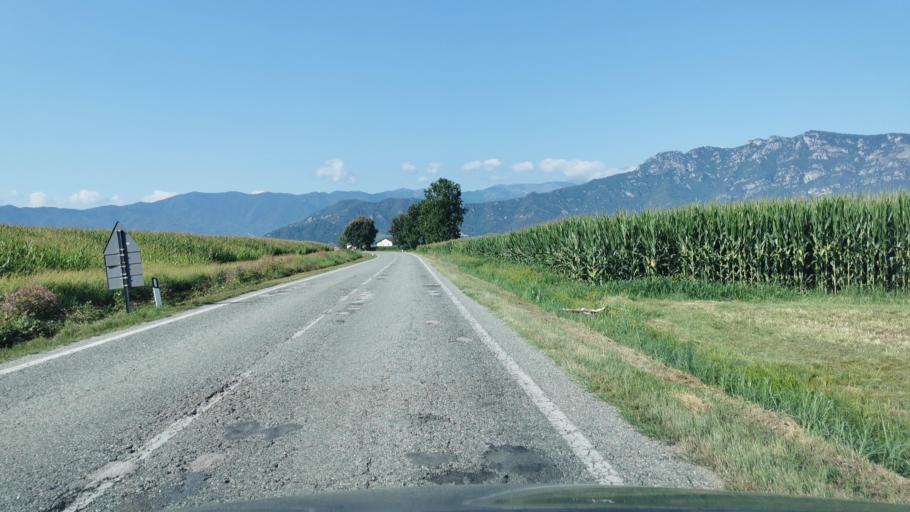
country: IT
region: Piedmont
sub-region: Provincia di Cuneo
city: Revello
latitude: 44.6958
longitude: 7.4273
